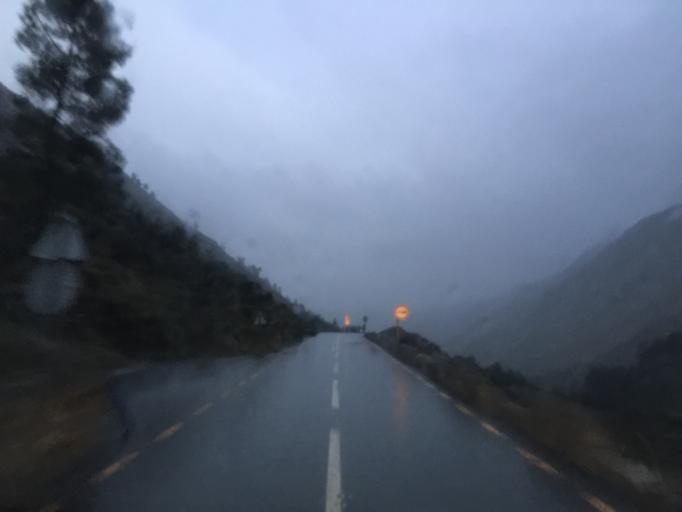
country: PT
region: Guarda
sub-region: Manteigas
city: Manteigas
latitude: 40.3596
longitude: -7.5554
